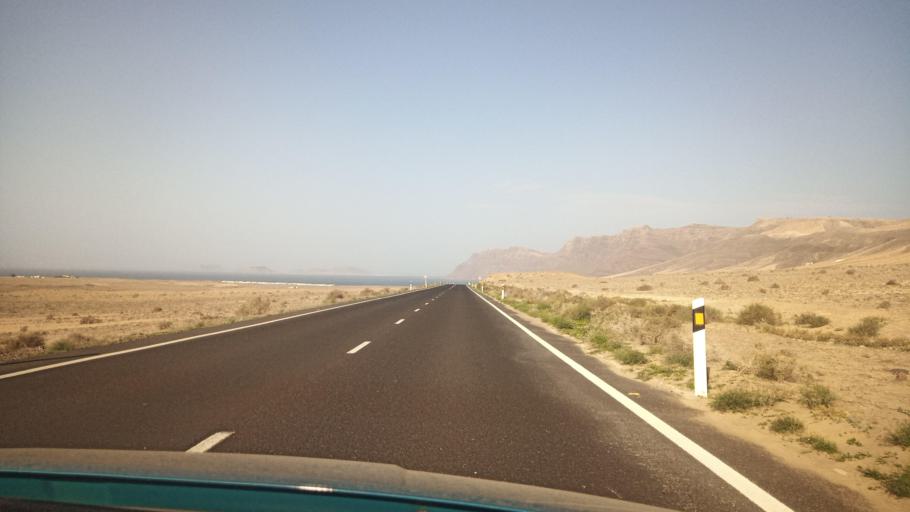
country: ES
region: Canary Islands
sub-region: Provincia de Las Palmas
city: Teguise
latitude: 29.0759
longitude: -13.5781
